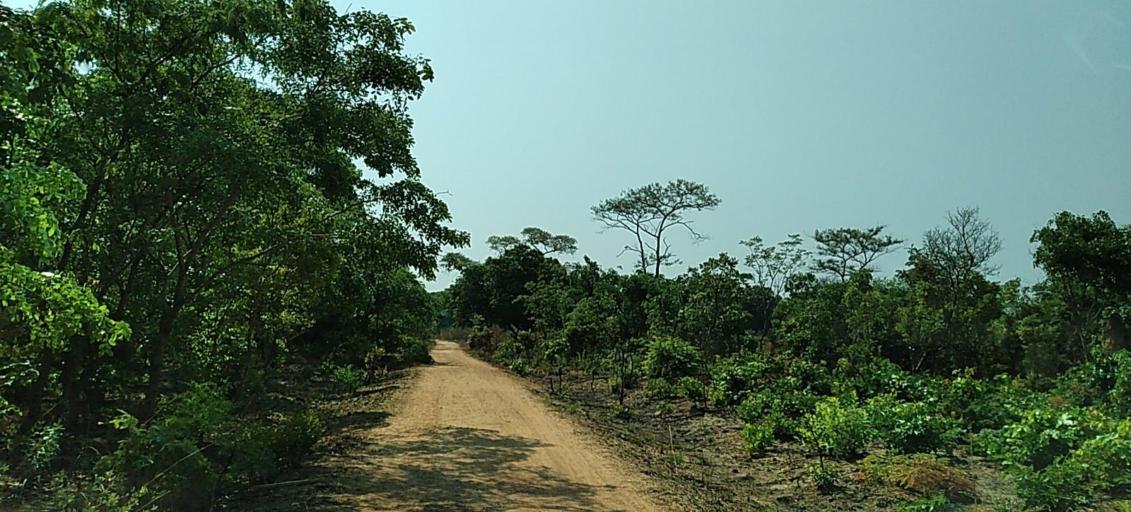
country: ZM
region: Copperbelt
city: Luanshya
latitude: -13.2793
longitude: 28.3106
